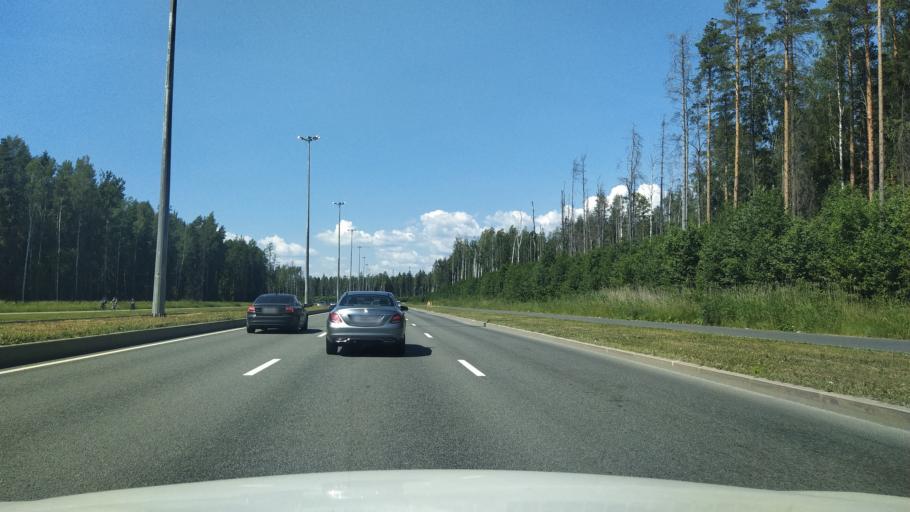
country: RU
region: St.-Petersburg
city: Levashovo
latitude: 60.0596
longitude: 30.2192
